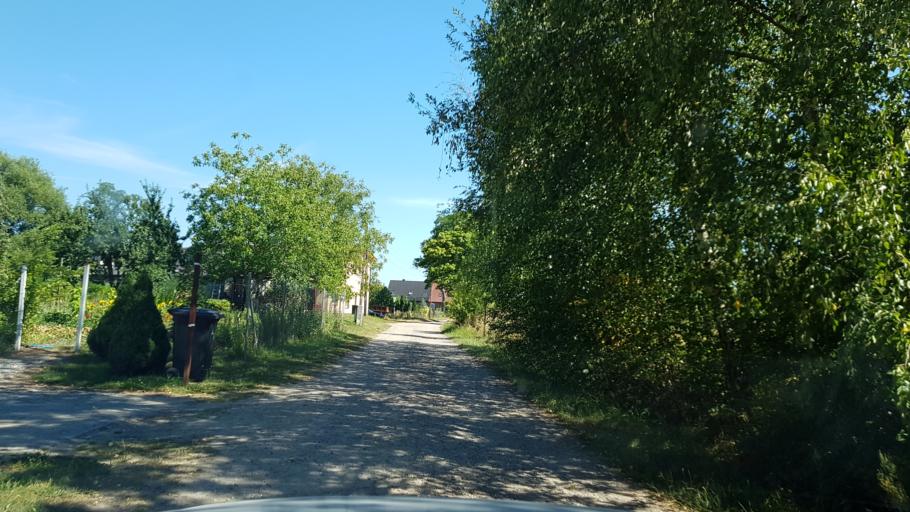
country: PL
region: West Pomeranian Voivodeship
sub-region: Powiat gryfinski
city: Moryn
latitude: 52.8990
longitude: 14.4115
